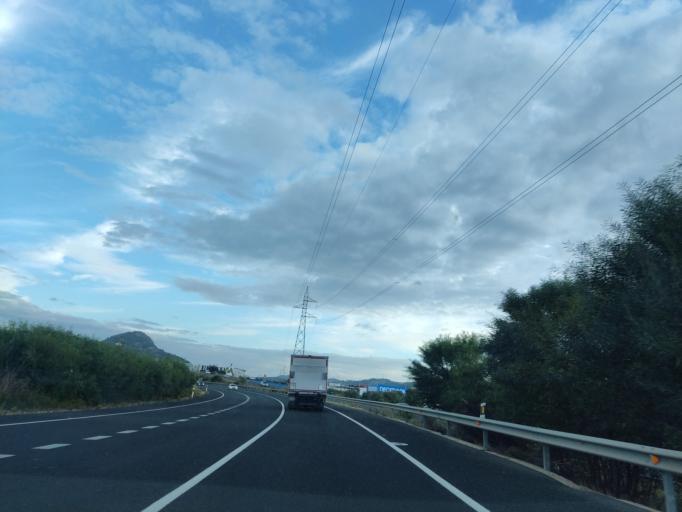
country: ES
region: Valencia
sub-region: Provincia de Alicante
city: Ondara
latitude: 38.8209
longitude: 0.0164
